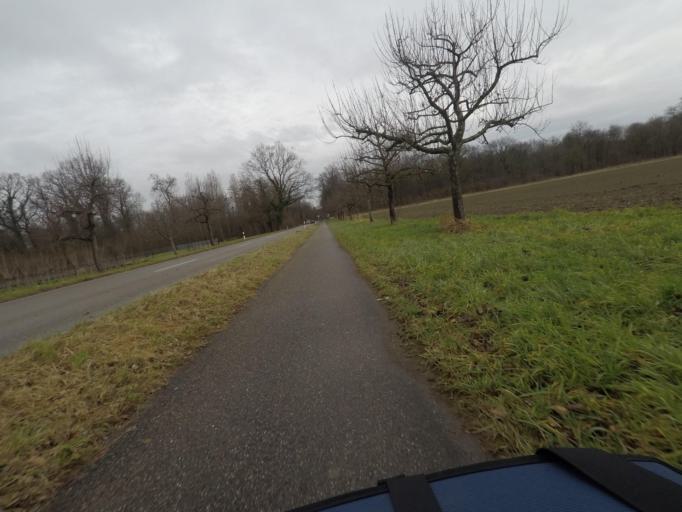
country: DE
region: Baden-Wuerttemberg
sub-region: Karlsruhe Region
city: Au am Rhein
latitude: 48.9625
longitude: 8.2493
